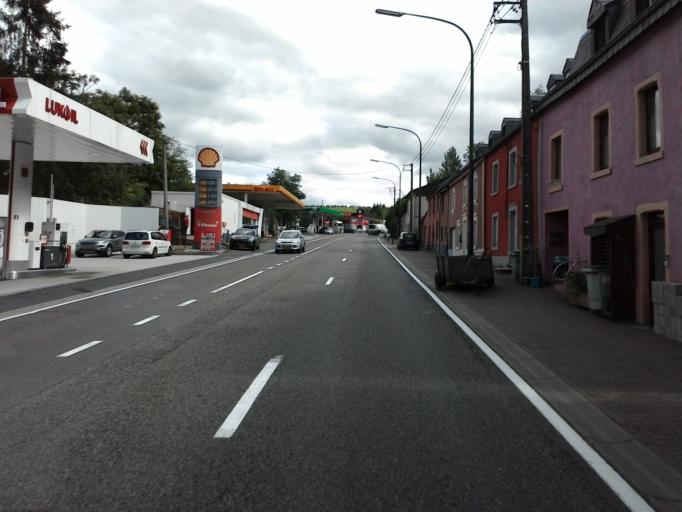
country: BE
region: Wallonia
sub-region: Province du Luxembourg
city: Martelange
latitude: 49.8294
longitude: 5.7448
